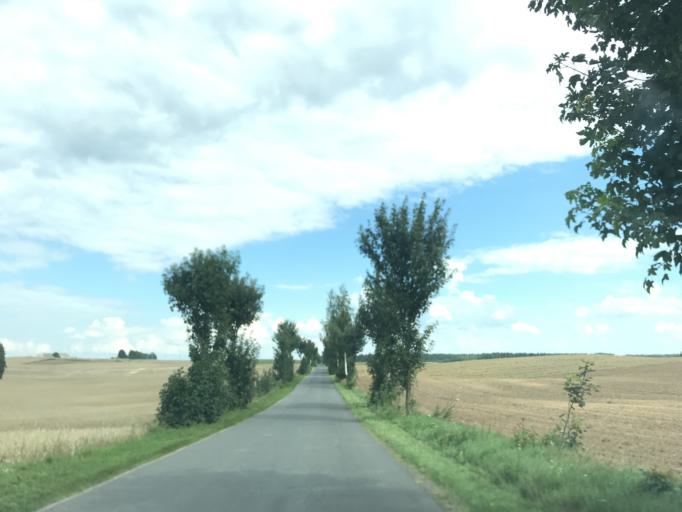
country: PL
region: Kujawsko-Pomorskie
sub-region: Powiat brodnicki
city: Brzozie
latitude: 53.3295
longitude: 19.6704
